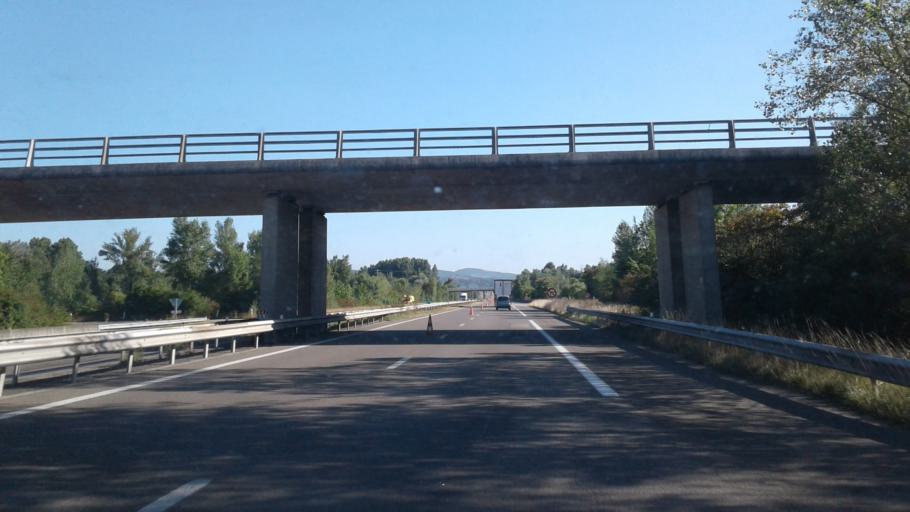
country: FR
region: Rhone-Alpes
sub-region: Departement de l'Ain
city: Ambronay
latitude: 46.0450
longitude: 5.3249
